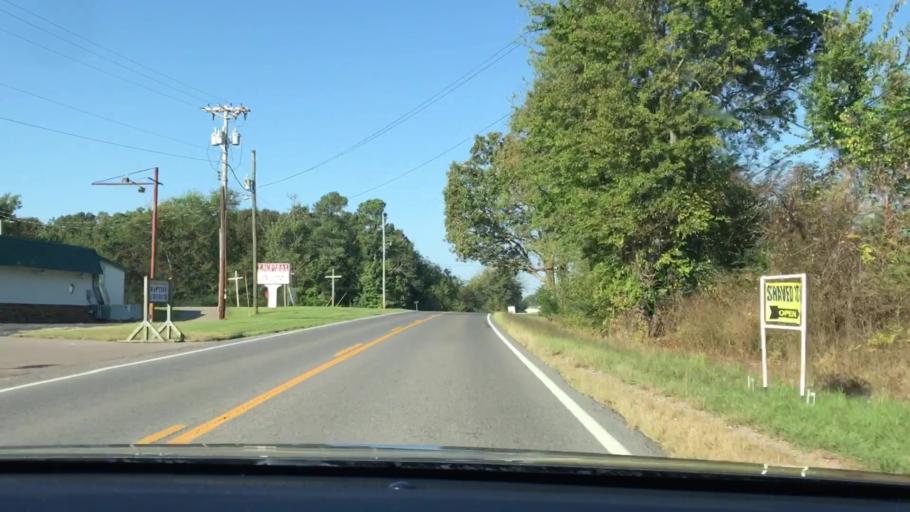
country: US
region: Kentucky
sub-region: Marshall County
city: Benton
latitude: 36.7769
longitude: -88.1530
